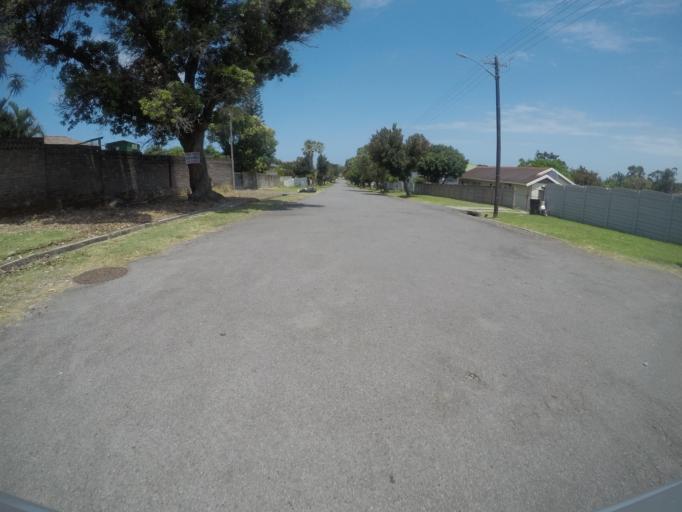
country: ZA
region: Eastern Cape
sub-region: Buffalo City Metropolitan Municipality
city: East London
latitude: -32.9760
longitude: 27.8832
